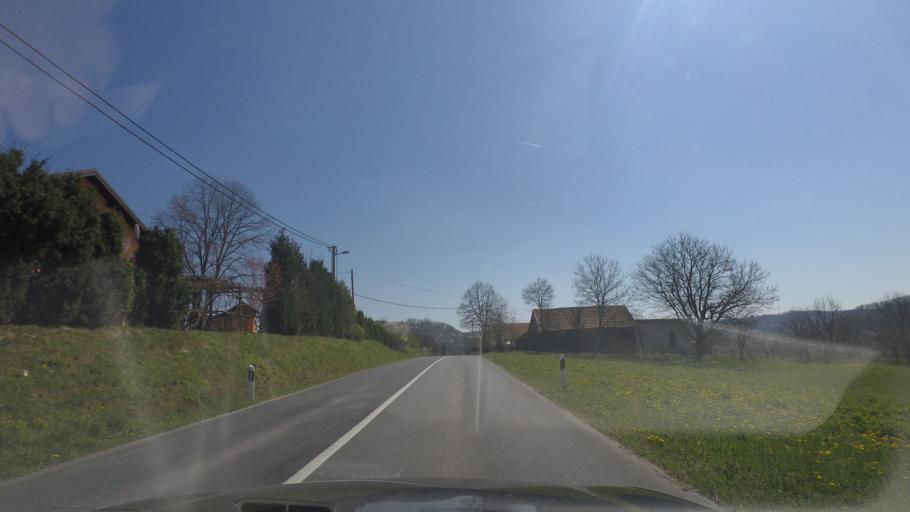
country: HR
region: Karlovacka
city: Vojnic
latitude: 45.3431
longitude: 15.6855
